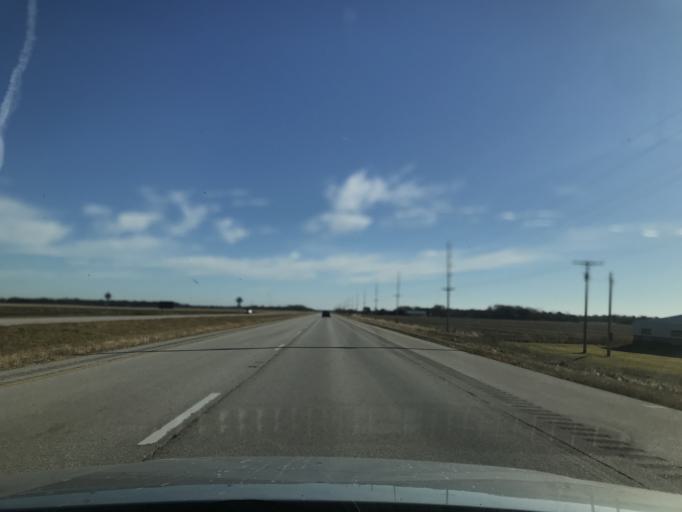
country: US
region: Illinois
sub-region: Hancock County
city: Carthage
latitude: 40.4152
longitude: -91.0608
